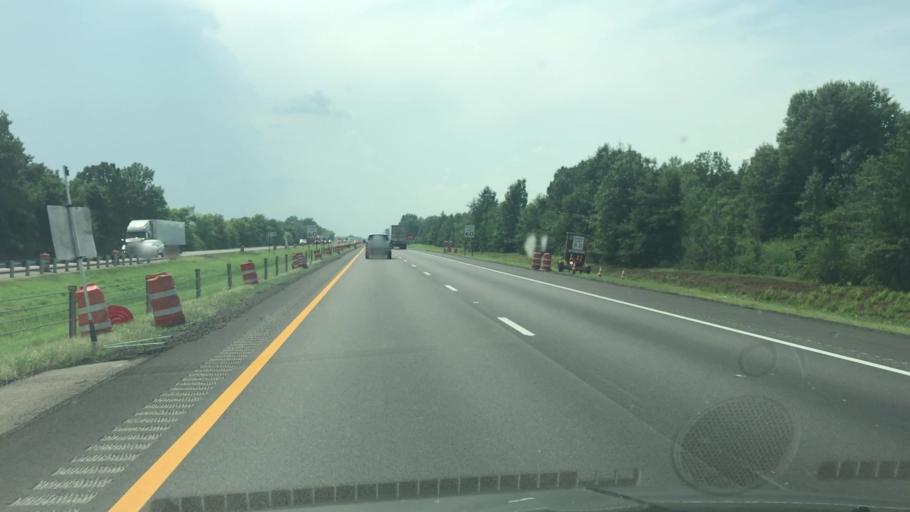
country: US
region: Arkansas
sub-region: Crittenden County
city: Earle
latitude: 35.1342
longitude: -90.4451
